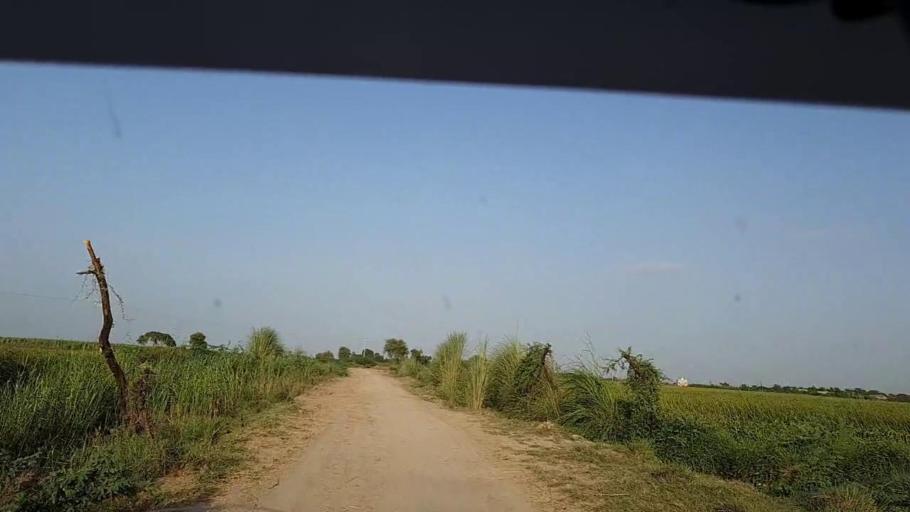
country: PK
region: Sindh
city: Badin
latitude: 24.5517
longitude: 68.8640
